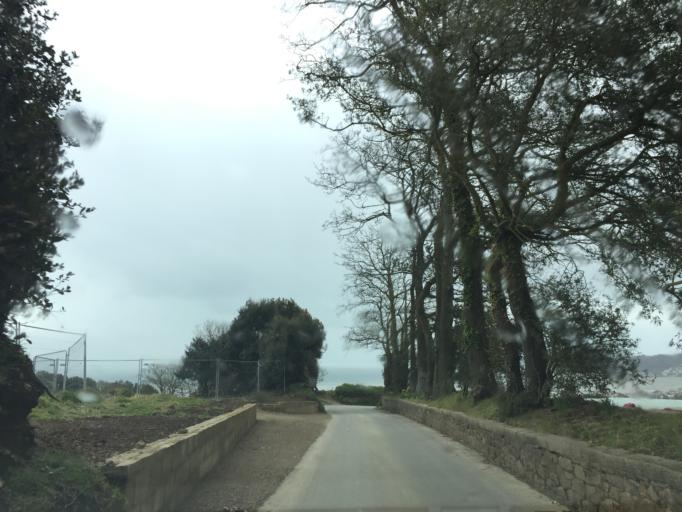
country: JE
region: St Helier
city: Saint Helier
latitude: 49.2042
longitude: -2.1494
